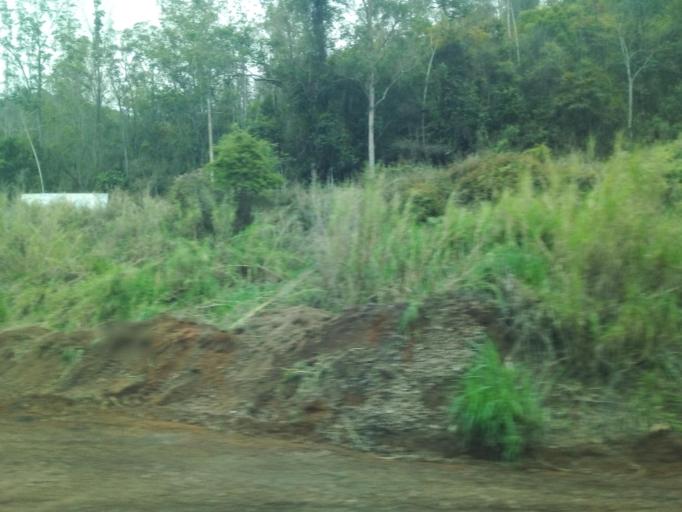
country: BR
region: Minas Gerais
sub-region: Rio Piracicaba
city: Rio Piracicaba
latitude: -19.8799
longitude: -43.1279
